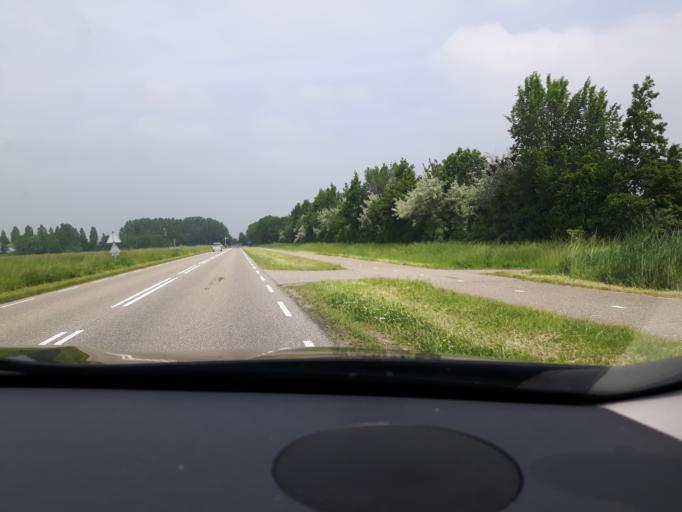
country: NL
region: Zeeland
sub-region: Gemeente Goes
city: Goes
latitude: 51.4477
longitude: 3.8924
